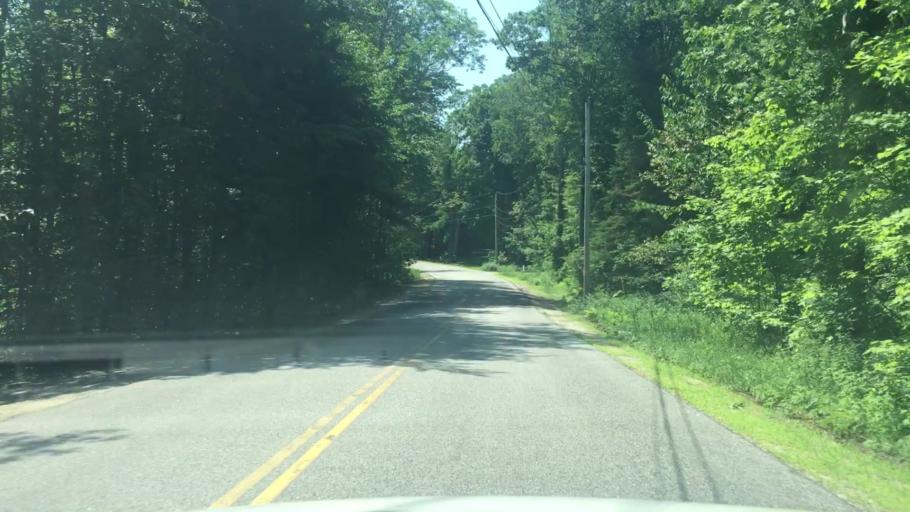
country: US
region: Maine
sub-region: Cumberland County
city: Cumberland Center
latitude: 43.8415
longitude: -70.3103
